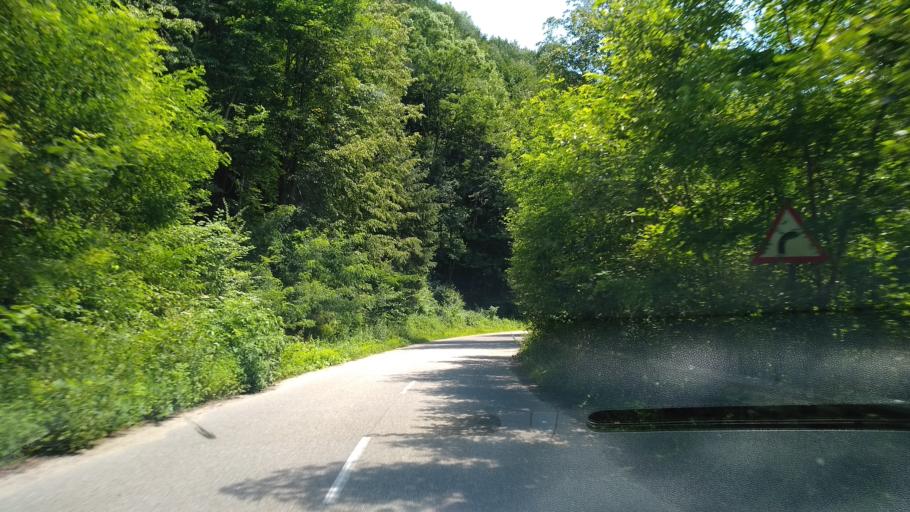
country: RO
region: Hunedoara
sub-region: Comuna Orastioara de Sus
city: Orastioara de Sus
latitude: 45.6449
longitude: 23.1948
